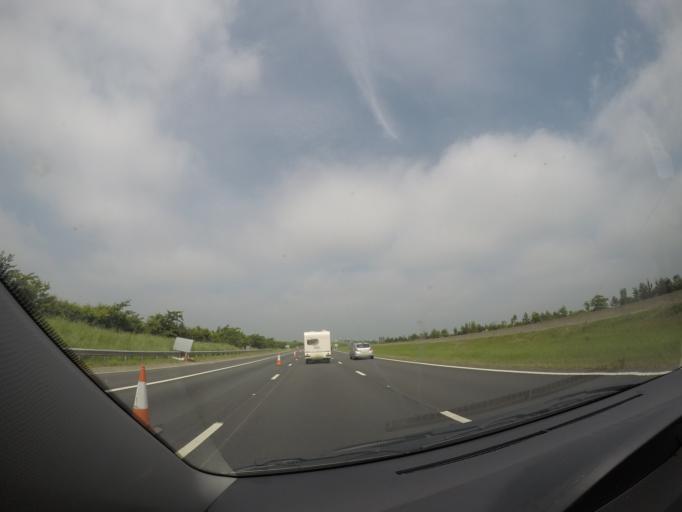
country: GB
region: England
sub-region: North Yorkshire
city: Ripon
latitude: 54.1680
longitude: -1.4506
